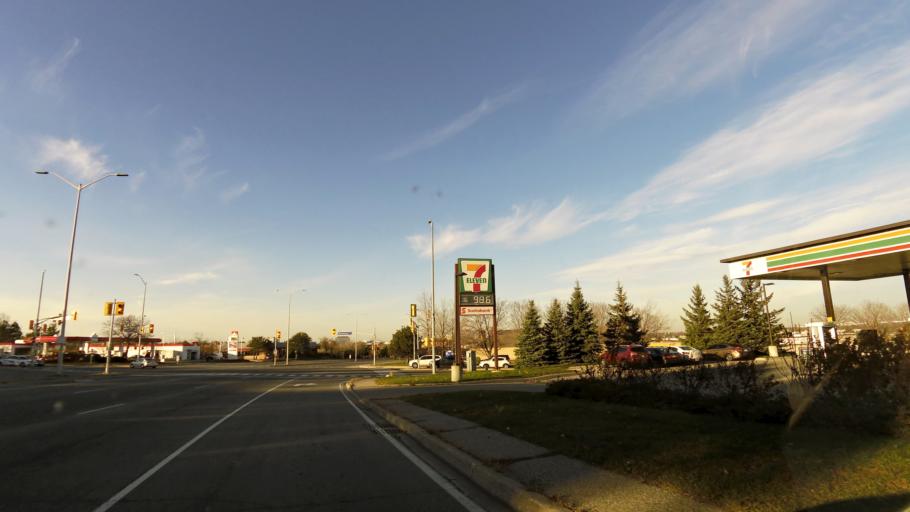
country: CA
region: Ontario
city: Mississauga
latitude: 43.5852
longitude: -79.7419
